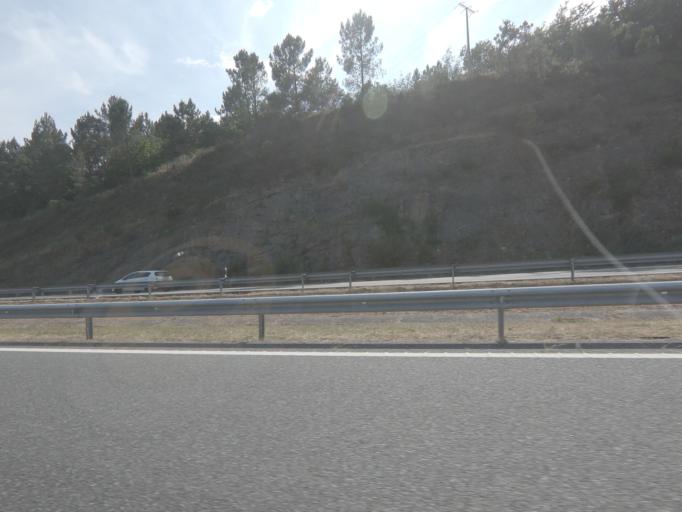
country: ES
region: Galicia
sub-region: Provincia de Ourense
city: Cenlle
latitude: 42.3225
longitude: -8.0762
